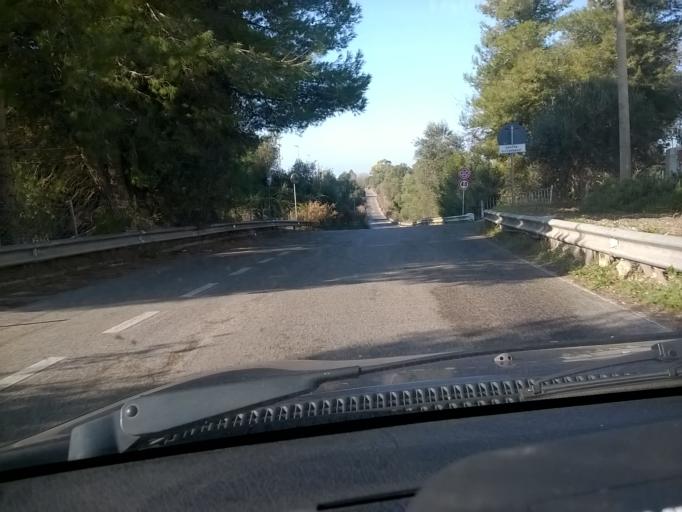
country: IT
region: Apulia
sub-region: Provincia di Taranto
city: Paolo VI
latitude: 40.4664
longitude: 17.2879
